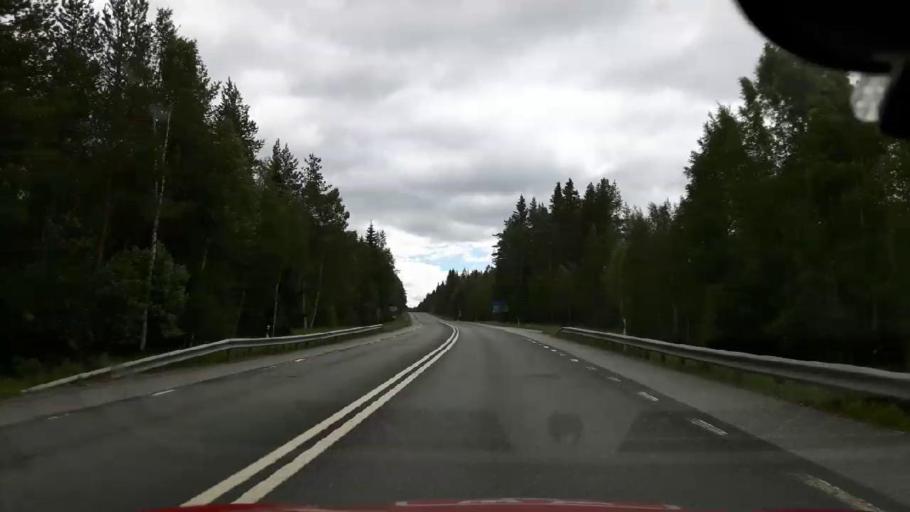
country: SE
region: Jaemtland
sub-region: Braecke Kommun
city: Braecke
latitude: 62.7153
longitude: 15.4608
